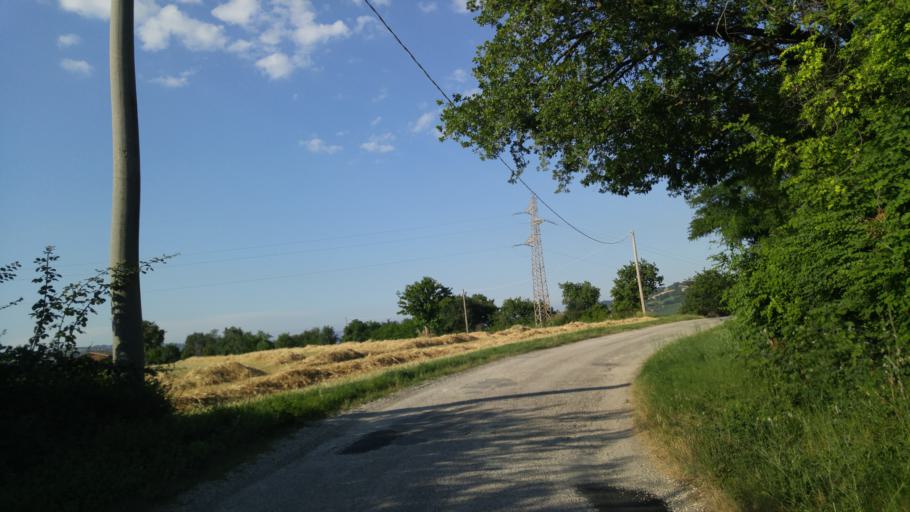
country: IT
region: The Marches
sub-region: Provincia di Pesaro e Urbino
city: Sant'Ippolito
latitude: 43.6989
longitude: 12.8775
